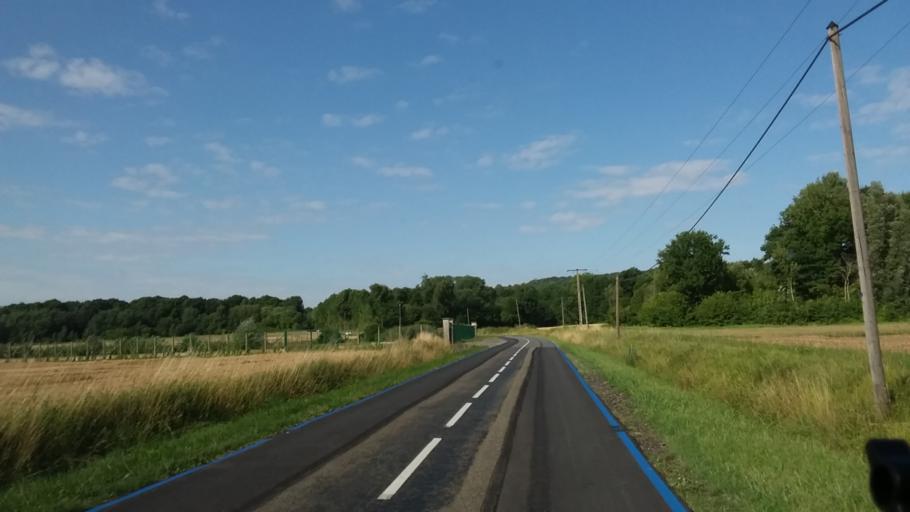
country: FR
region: Picardie
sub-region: Departement de l'Aisne
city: Saint-Erme-Outre-et-Ramecourt
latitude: 49.4564
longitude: 3.8140
